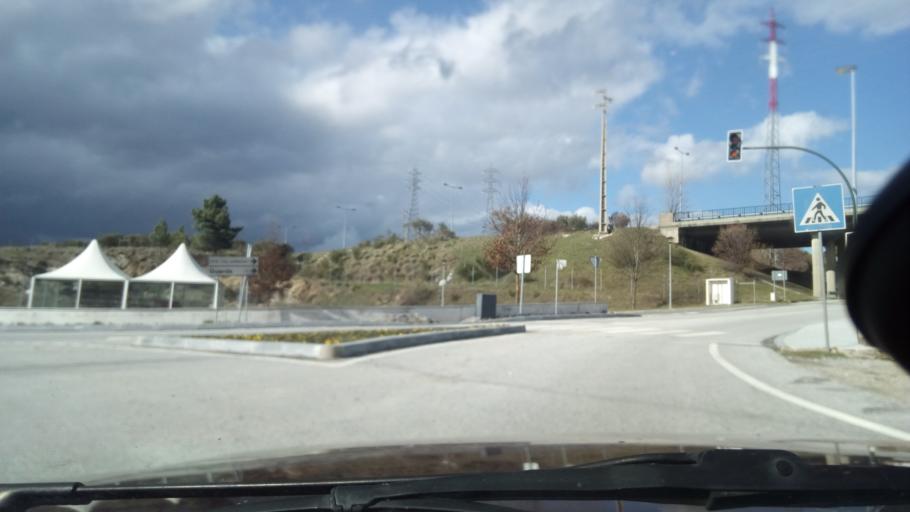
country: PT
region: Guarda
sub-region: Guarda
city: Guarda
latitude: 40.5352
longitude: -7.2886
